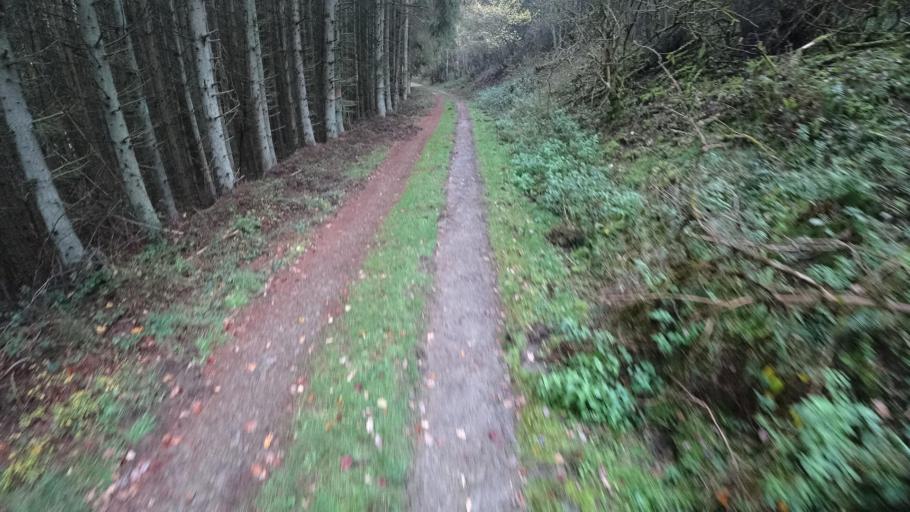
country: DE
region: Rheinland-Pfalz
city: Honningen
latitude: 50.4653
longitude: 6.9341
